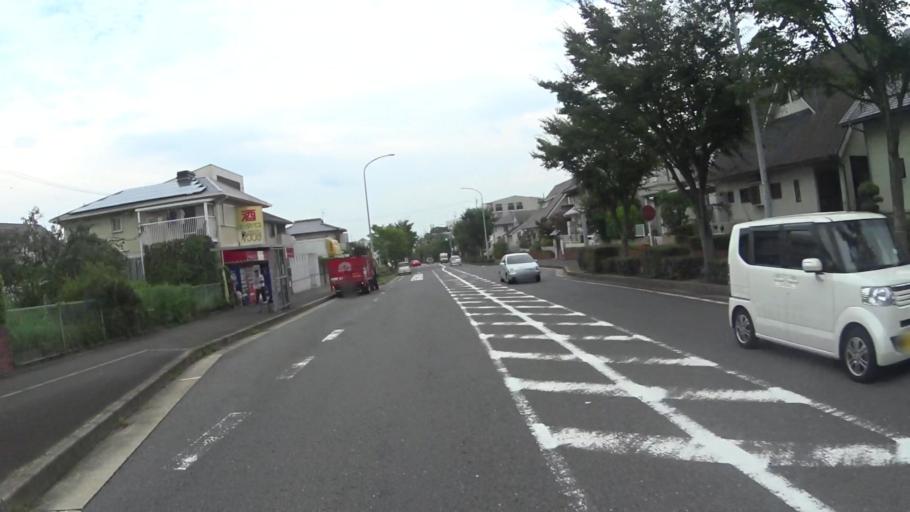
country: JP
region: Nara
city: Nara-shi
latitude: 34.7244
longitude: 135.7788
